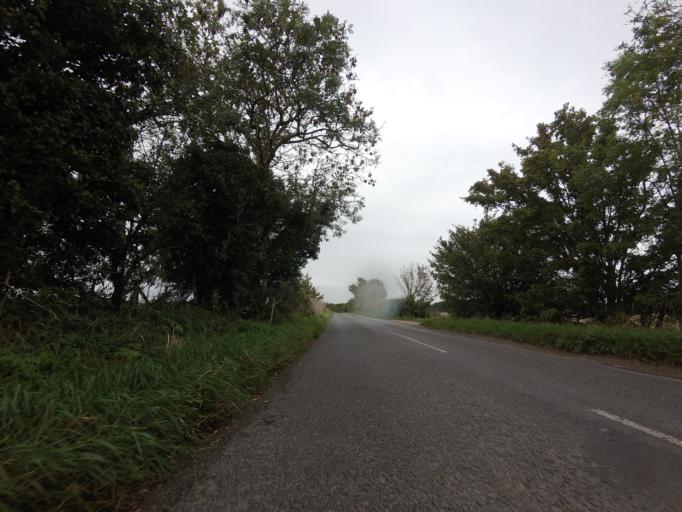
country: GB
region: England
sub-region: Cambridgeshire
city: Harston
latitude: 52.0830
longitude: 0.0792
